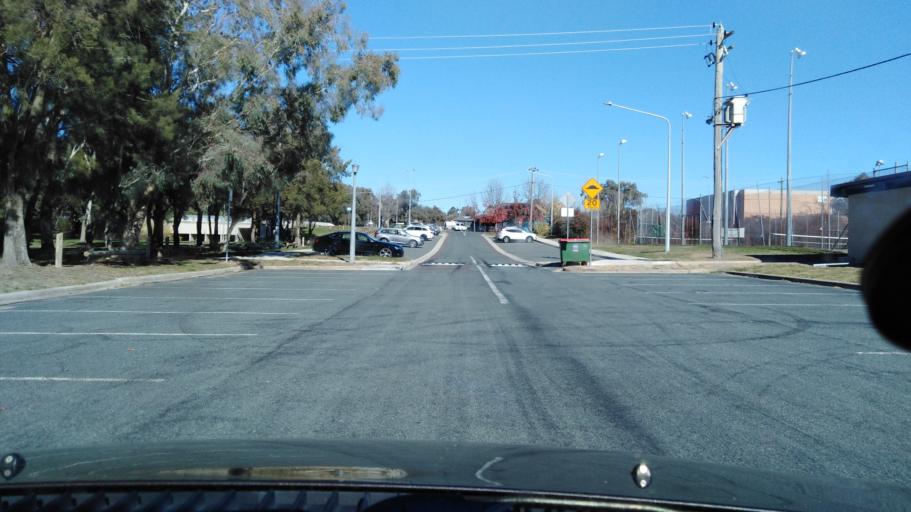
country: AU
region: Australian Capital Territory
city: Forrest
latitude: -35.3382
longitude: 149.0535
